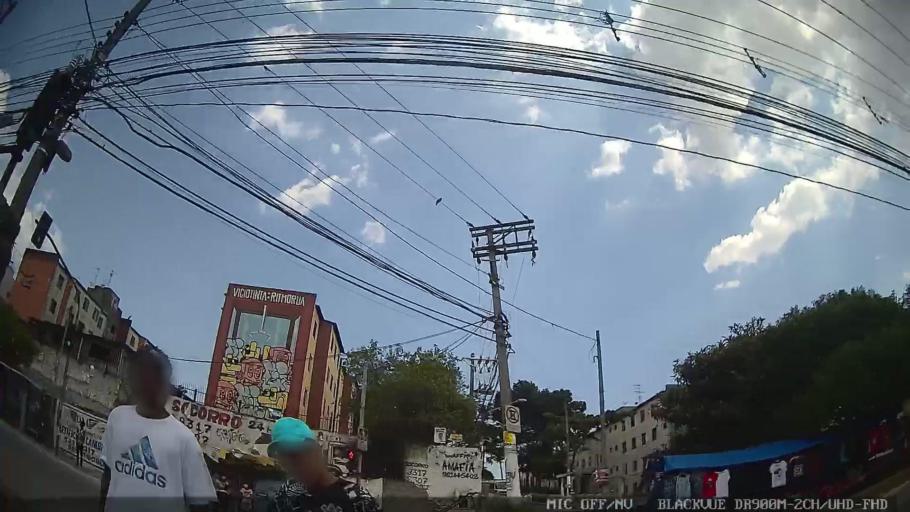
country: BR
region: Sao Paulo
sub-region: Taboao Da Serra
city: Taboao da Serra
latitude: -23.6620
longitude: -46.7796
